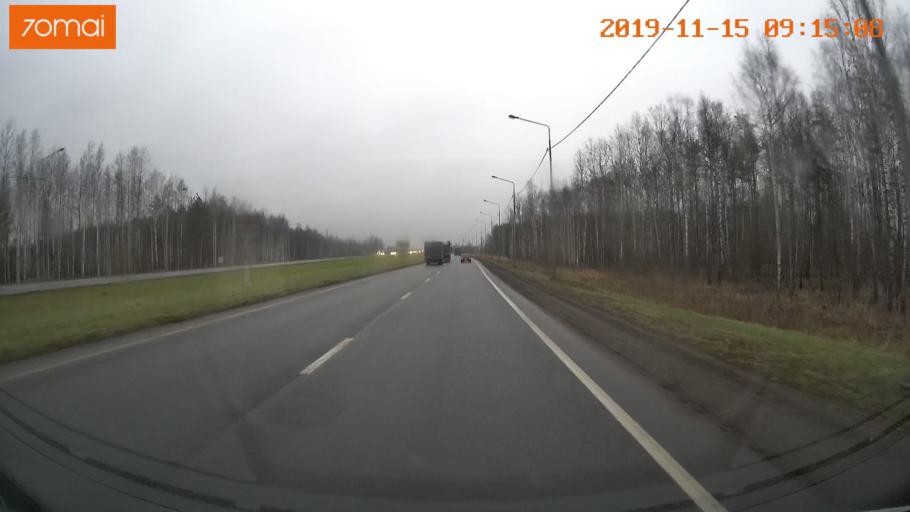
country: RU
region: Vologda
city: Tonshalovo
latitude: 59.2352
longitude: 37.9647
